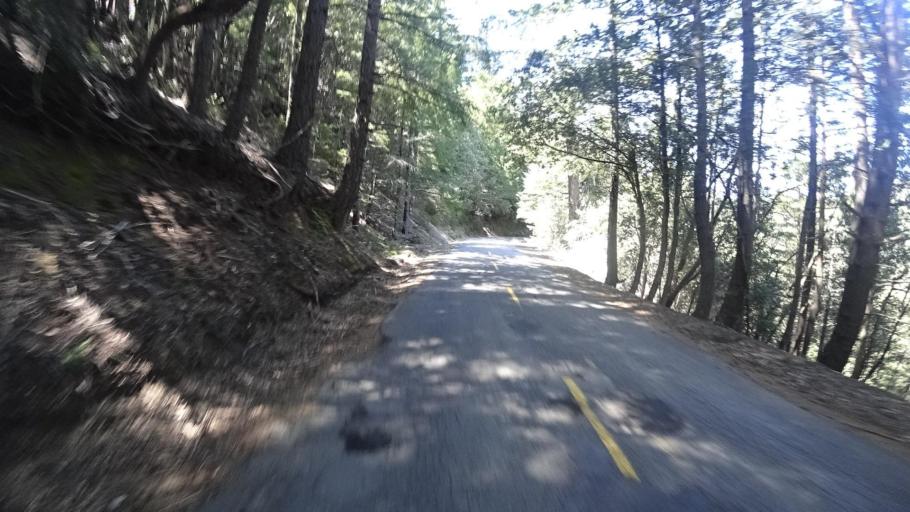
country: US
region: California
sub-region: Humboldt County
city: Rio Dell
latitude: 40.2687
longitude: -124.0772
